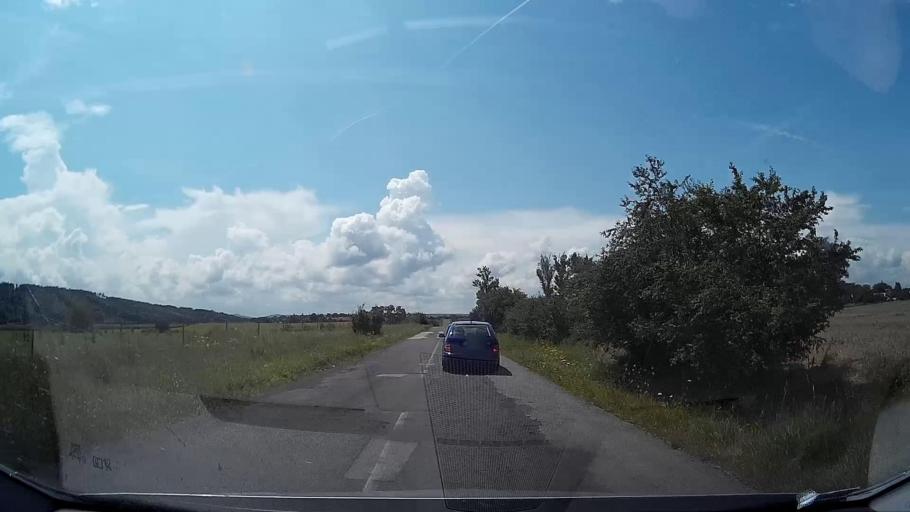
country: SK
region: Banskobystricky
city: Fil'akovo
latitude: 48.3341
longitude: 19.8213
